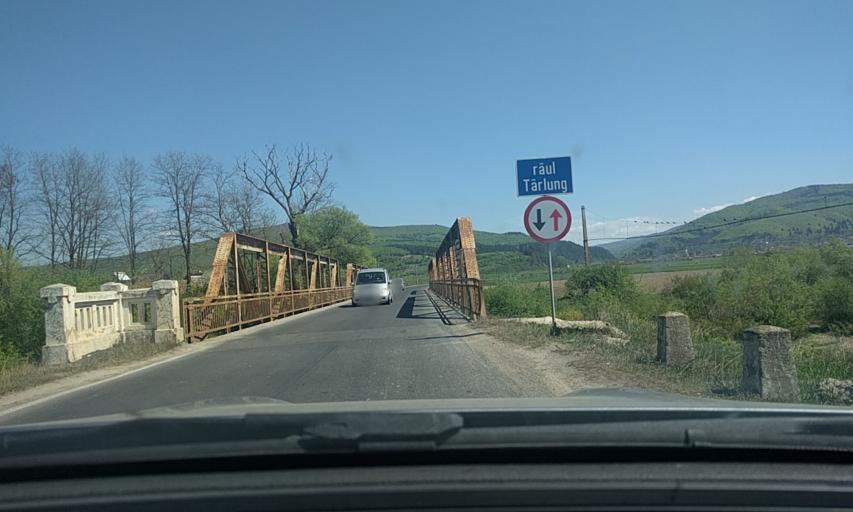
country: RO
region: Brasov
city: Tunelu-Teliu
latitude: 45.7110
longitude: 25.8262
